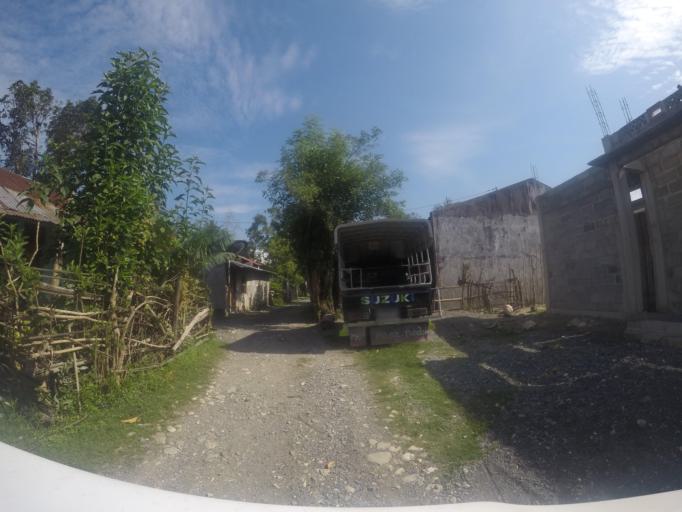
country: TL
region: Viqueque
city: Viqueque
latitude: -8.8561
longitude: 126.3617
